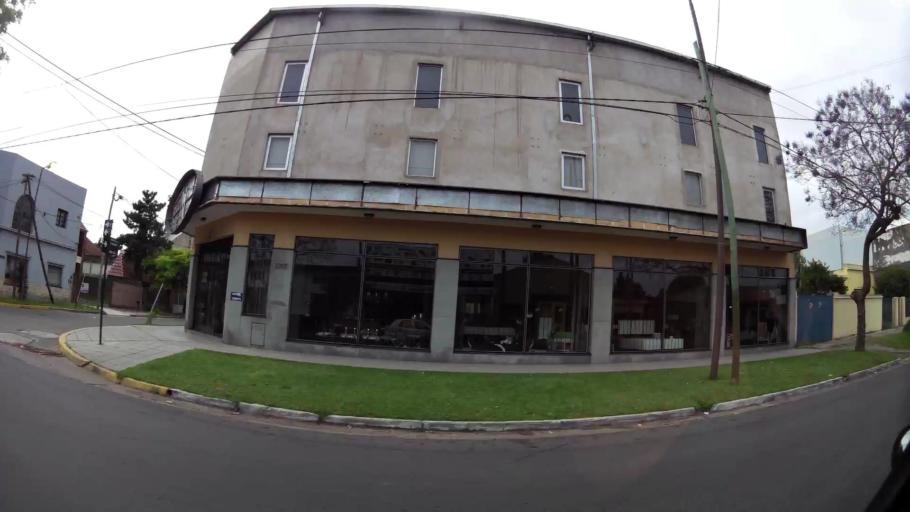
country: AR
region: Buenos Aires
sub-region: Partido de Quilmes
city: Quilmes
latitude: -34.7362
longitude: -58.2683
